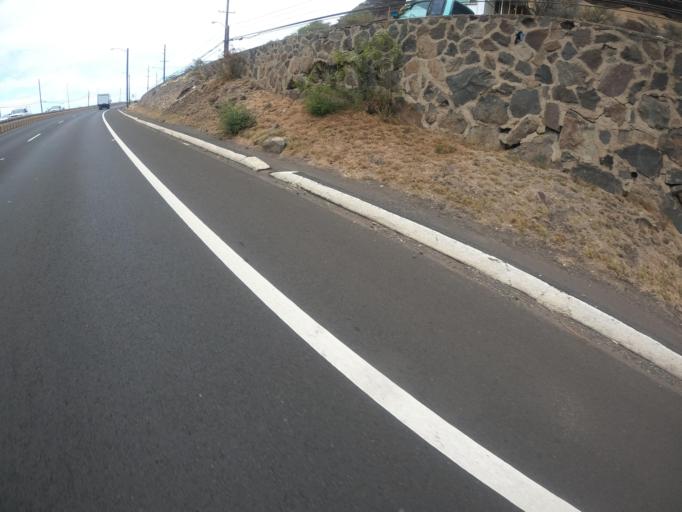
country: US
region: Hawaii
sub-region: Honolulu County
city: Nanakuli
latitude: 21.3987
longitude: -158.1716
